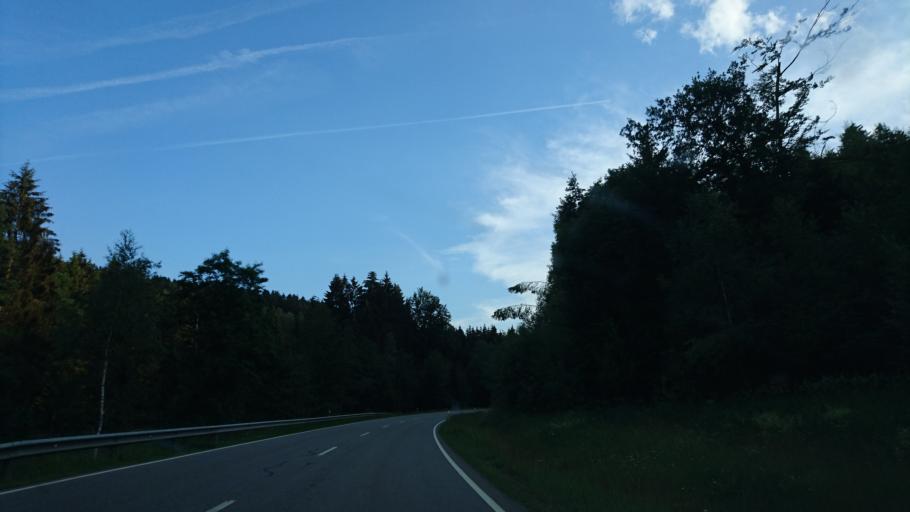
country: DE
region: Bavaria
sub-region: Lower Bavaria
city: Grafenau
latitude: 48.8733
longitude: 13.3966
